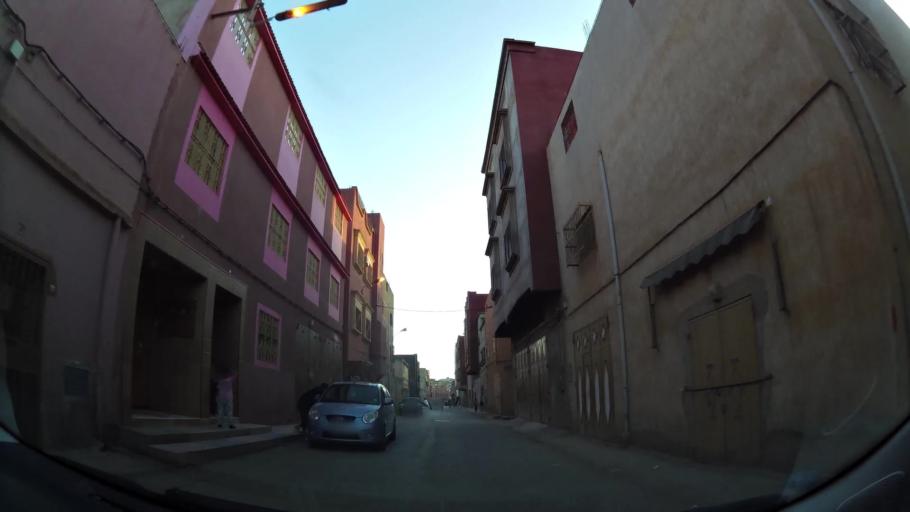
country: MA
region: Oriental
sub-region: Berkane-Taourirt
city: Berkane
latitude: 34.9195
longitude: -2.3165
